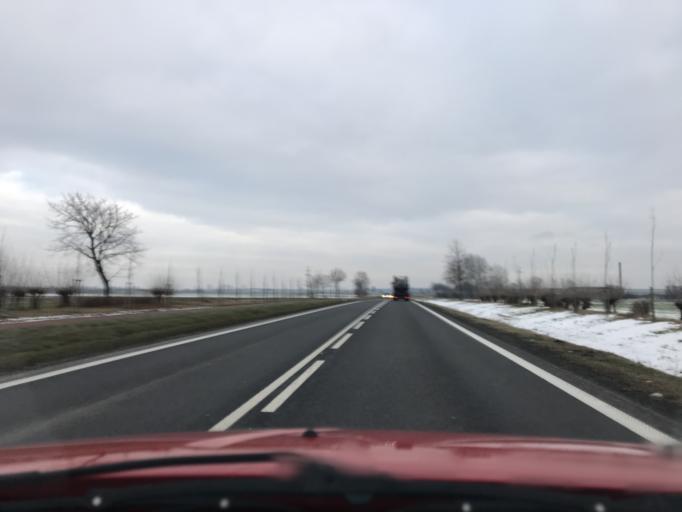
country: PL
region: Greater Poland Voivodeship
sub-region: Powiat pleszewski
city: Goluchow
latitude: 51.8807
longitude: 17.8732
